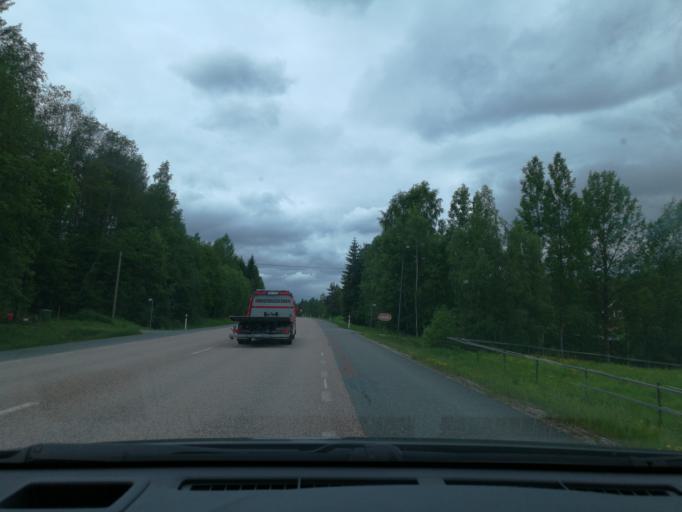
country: SE
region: Vaestmanland
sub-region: Fagersta Kommun
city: Fagersta
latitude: 59.9717
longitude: 15.7151
